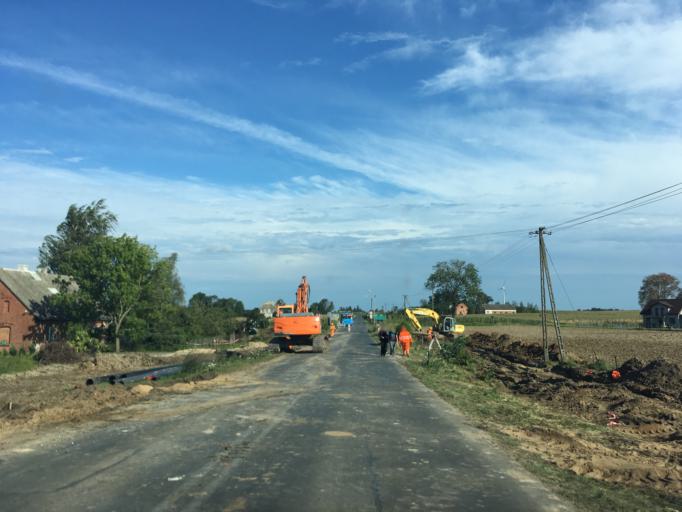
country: PL
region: Kujawsko-Pomorskie
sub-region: Powiat wabrzeski
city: Pluznica
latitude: 53.2908
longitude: 18.7983
